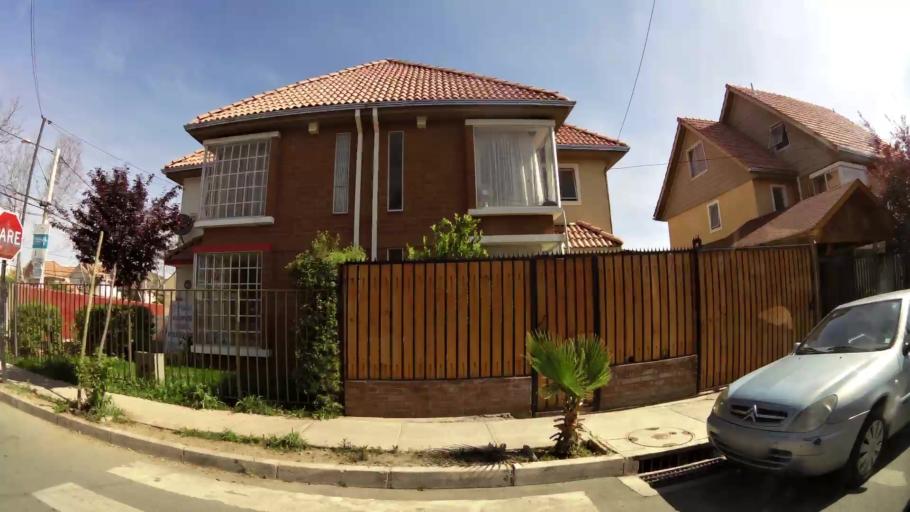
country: CL
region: Santiago Metropolitan
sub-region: Provincia de Cordillera
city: Puente Alto
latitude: -33.5925
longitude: -70.5439
